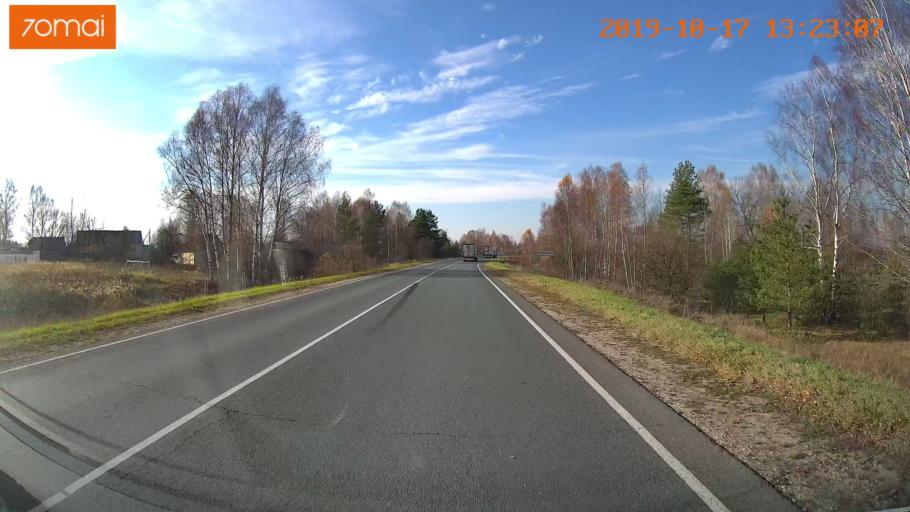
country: RU
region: Rjazan
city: Gus'-Zheleznyy
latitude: 55.0879
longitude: 40.9854
